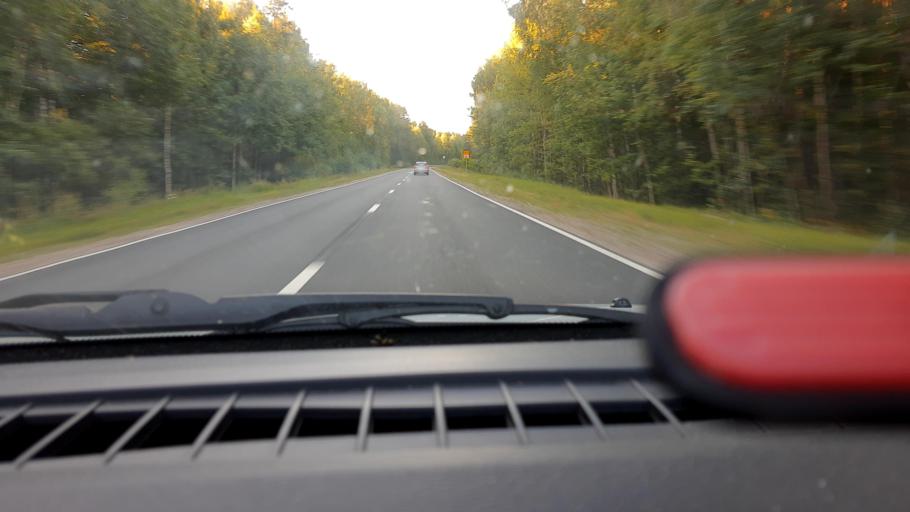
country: RU
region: Nizjnij Novgorod
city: Krasnyye Baki
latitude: 57.1277
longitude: 45.2121
